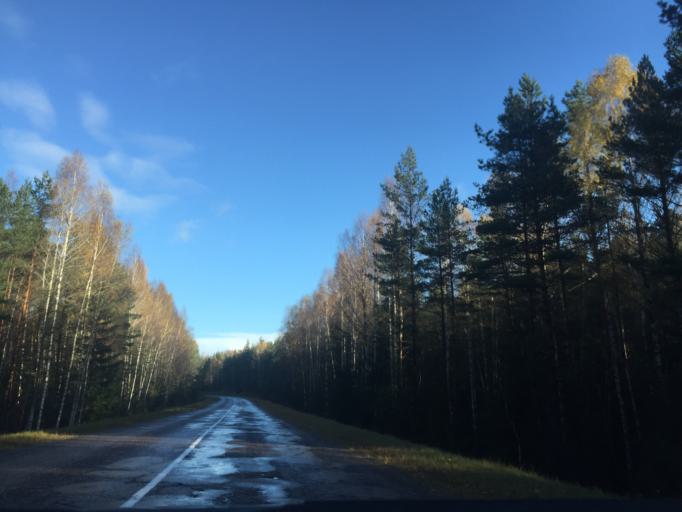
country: LV
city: Tireli
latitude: 56.8856
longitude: 23.5365
